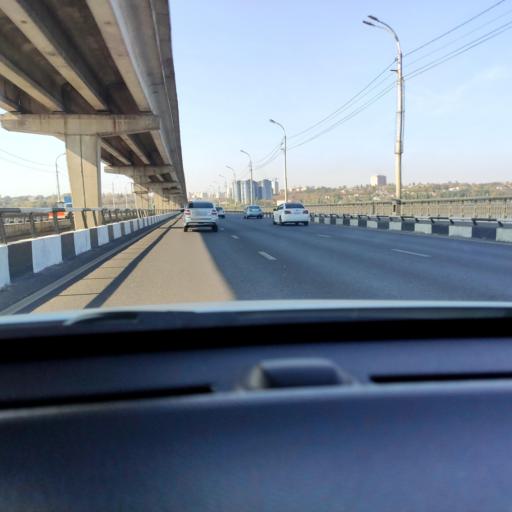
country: RU
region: Voronezj
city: Voronezh
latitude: 51.6897
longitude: 39.2456
